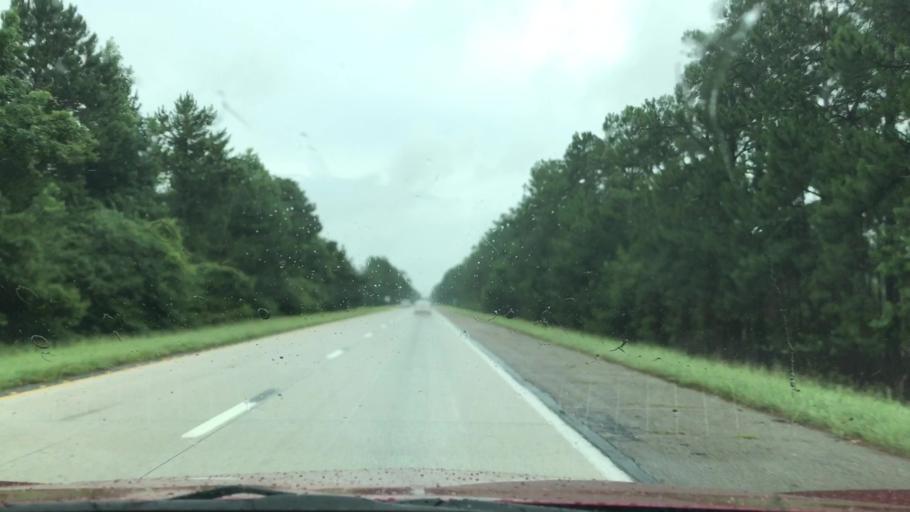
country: US
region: South Carolina
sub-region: Orangeburg County
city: Holly Hill
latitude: 33.2073
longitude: -80.4081
